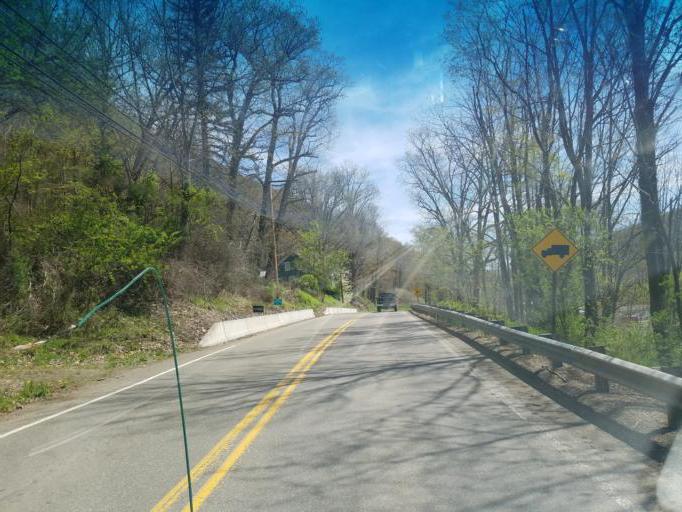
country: US
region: Pennsylvania
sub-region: Potter County
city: Galeton
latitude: 41.7378
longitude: -77.6385
